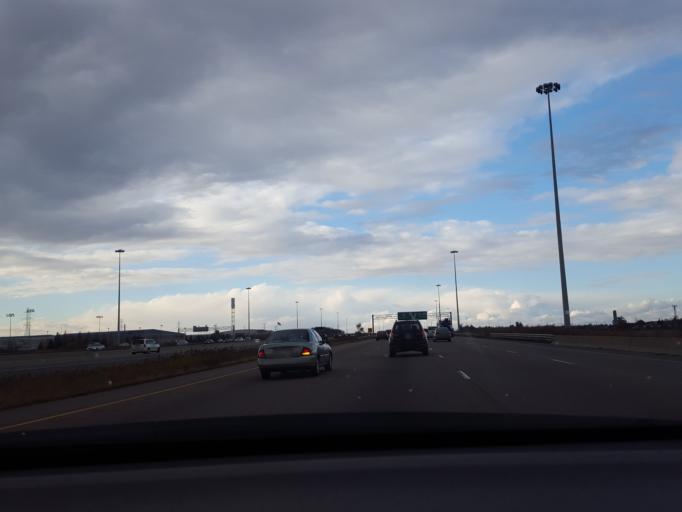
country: CA
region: Ontario
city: Mississauga
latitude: 43.6265
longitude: -79.6422
